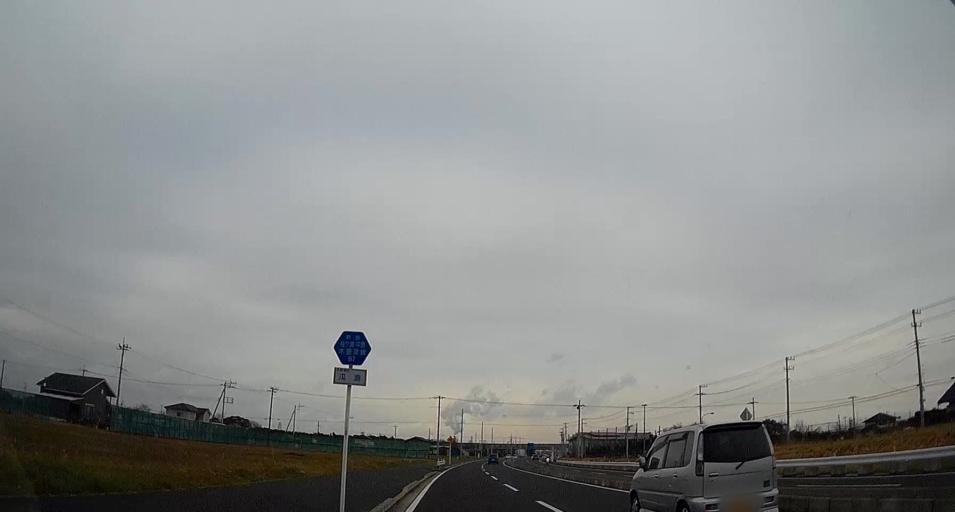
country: JP
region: Chiba
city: Kisarazu
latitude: 35.4266
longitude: 139.9234
